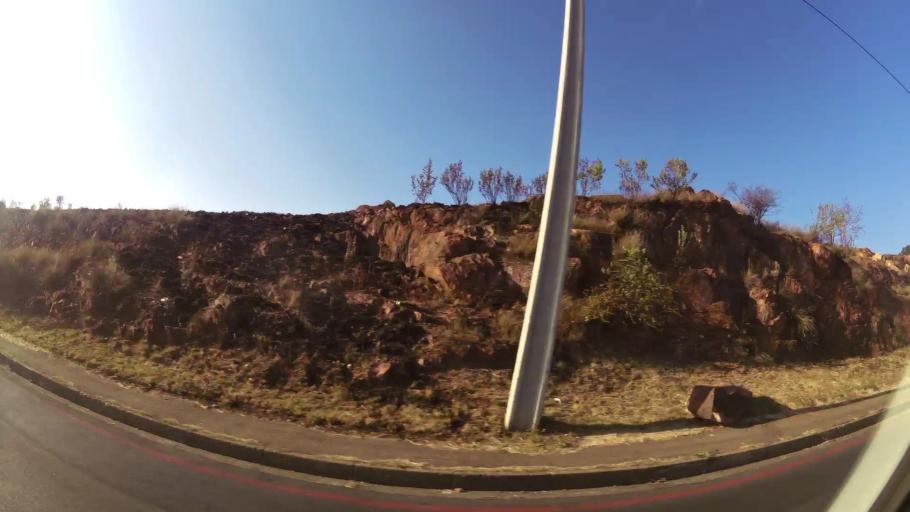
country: ZA
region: Gauteng
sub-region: Ekurhuleni Metropolitan Municipality
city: Germiston
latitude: -26.1777
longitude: 28.1583
